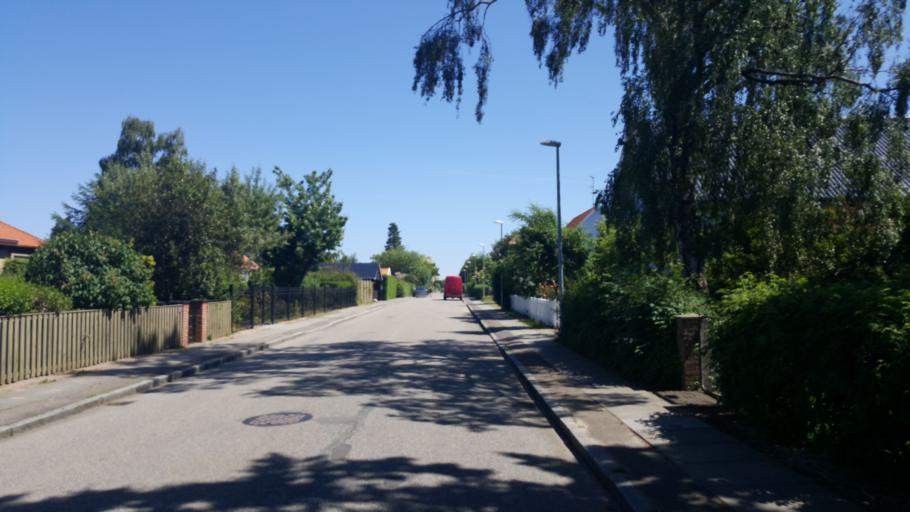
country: DK
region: Capital Region
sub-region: Tarnby Kommune
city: Tarnby
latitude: 55.6190
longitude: 12.6167
